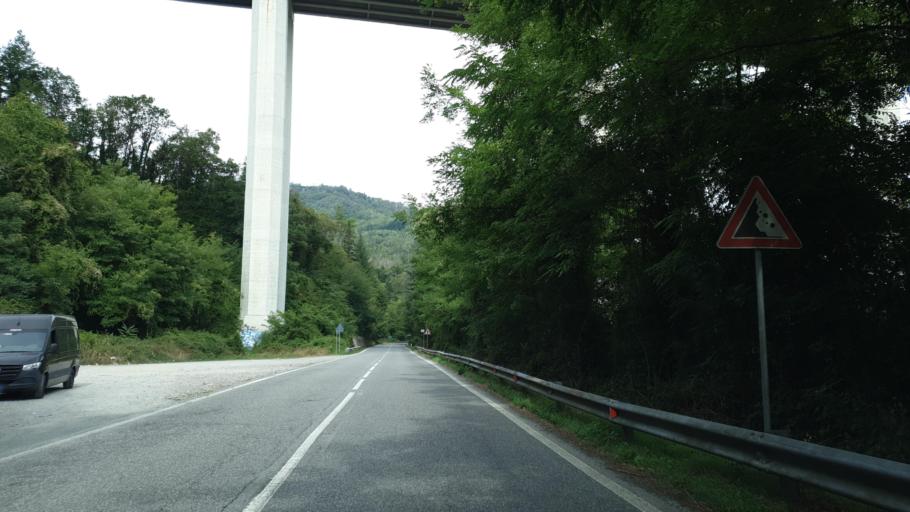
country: IT
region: Liguria
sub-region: Provincia di La Spezia
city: Carrodano
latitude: 44.2323
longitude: 9.6394
